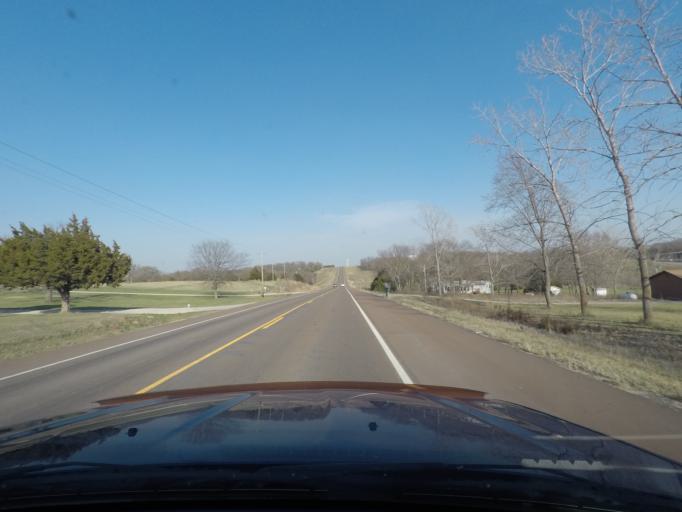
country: US
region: Kansas
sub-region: Douglas County
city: Lawrence
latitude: 39.0004
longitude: -95.3630
